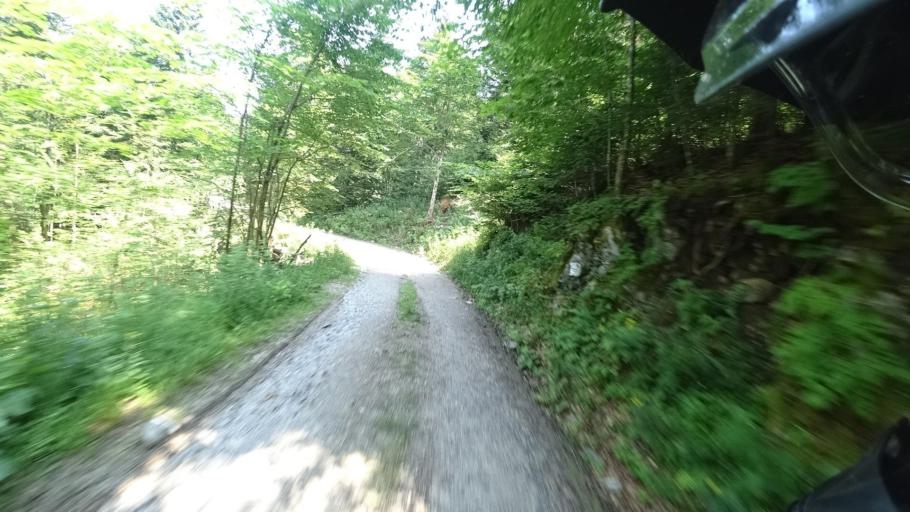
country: HR
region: Primorsko-Goranska
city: Vrbovsko
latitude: 45.3402
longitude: 15.0296
